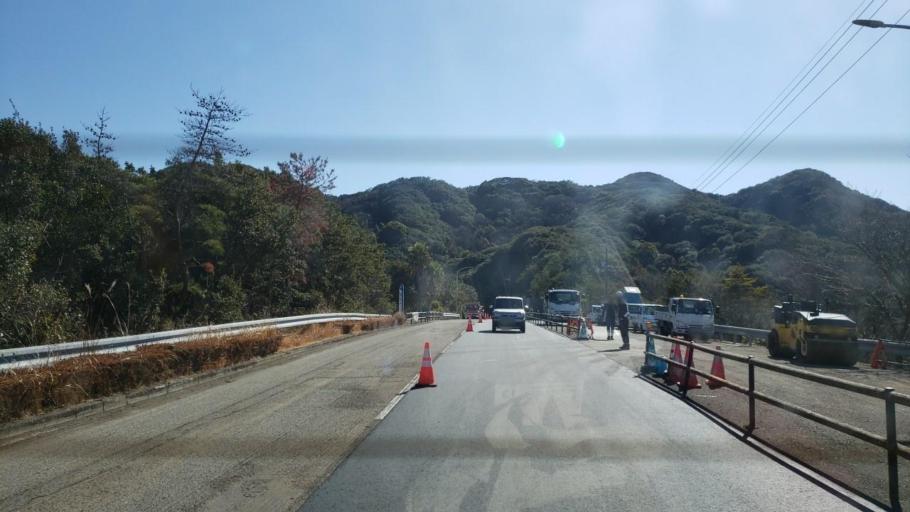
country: JP
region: Tokushima
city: Narutocho-mitsuishi
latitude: 34.2295
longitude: 134.6191
